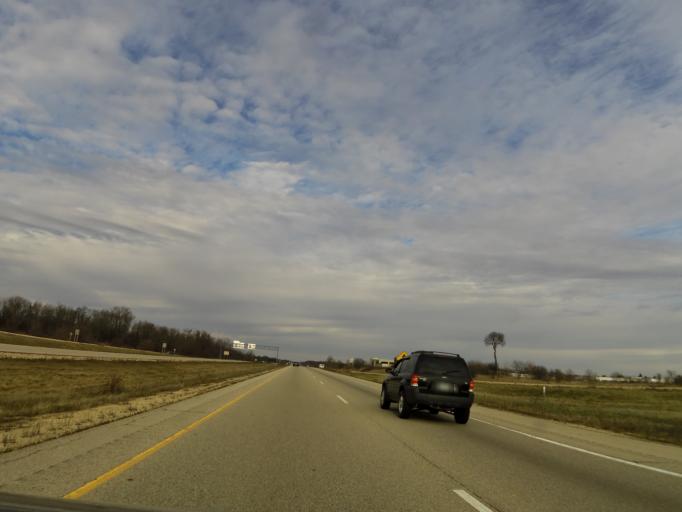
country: US
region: Wisconsin
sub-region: Rock County
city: Janesville
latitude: 42.6720
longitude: -88.9834
